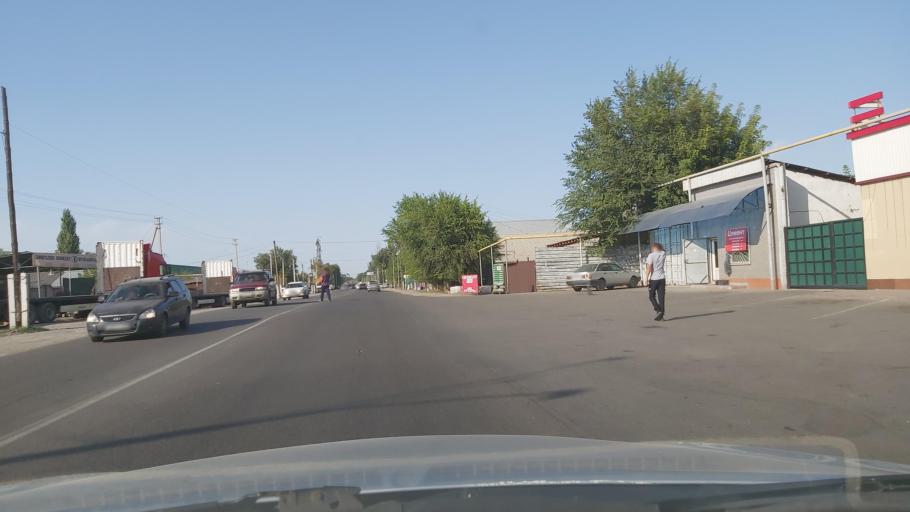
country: KZ
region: Almaty Oblysy
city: Energeticheskiy
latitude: 43.4777
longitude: 77.0316
